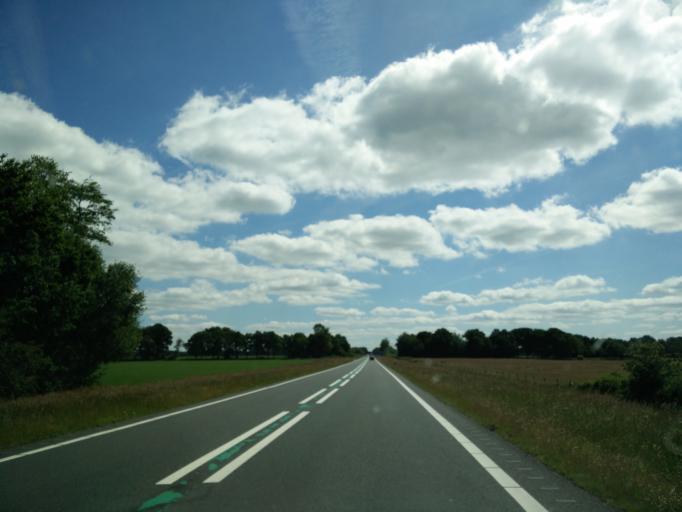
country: NL
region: Drenthe
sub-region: Gemeente Coevorden
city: Sleen
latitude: 52.8043
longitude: 6.7098
